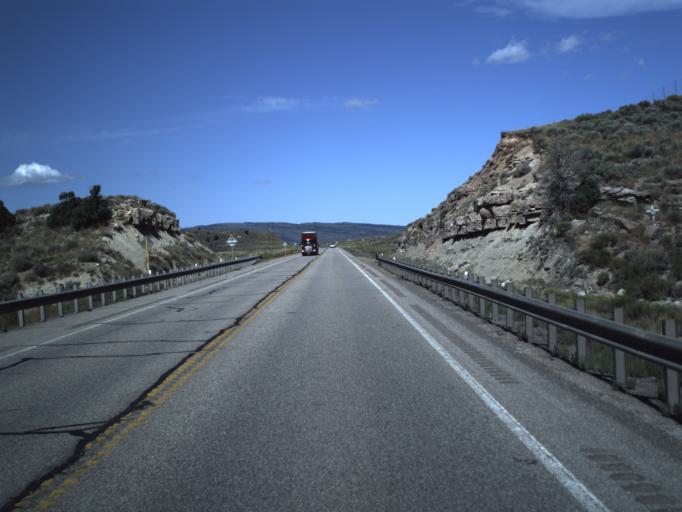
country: US
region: Utah
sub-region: Carbon County
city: Helper
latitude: 39.8263
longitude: -110.9532
